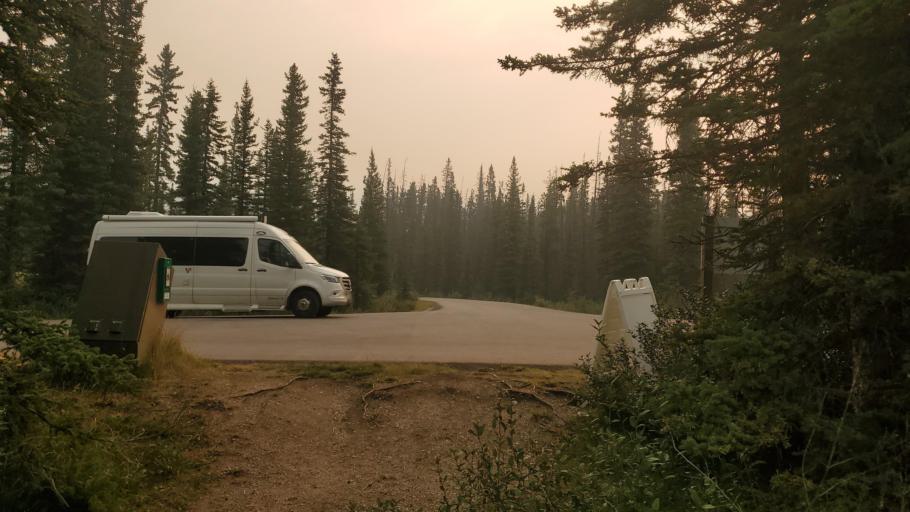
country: CA
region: Alberta
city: Banff
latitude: 51.2664
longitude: -115.9265
